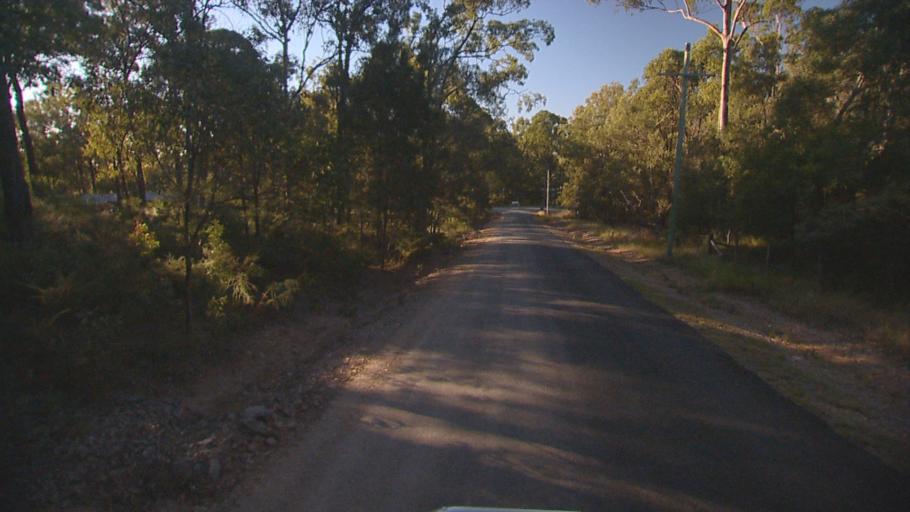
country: AU
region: Queensland
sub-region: Logan
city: Chambers Flat
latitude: -27.7639
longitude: 153.1334
